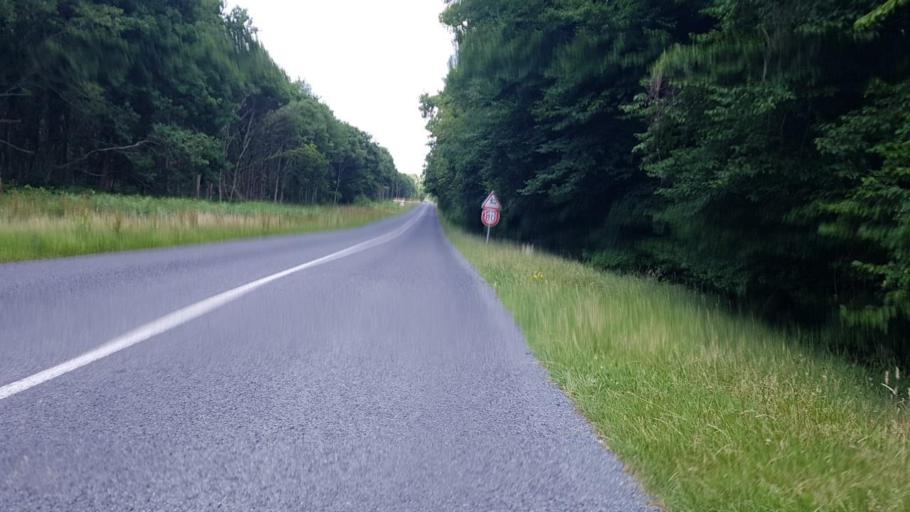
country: FR
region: Picardie
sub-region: Departement de l'Oise
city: Chiry-Ourscamp
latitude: 49.5296
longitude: 2.9843
